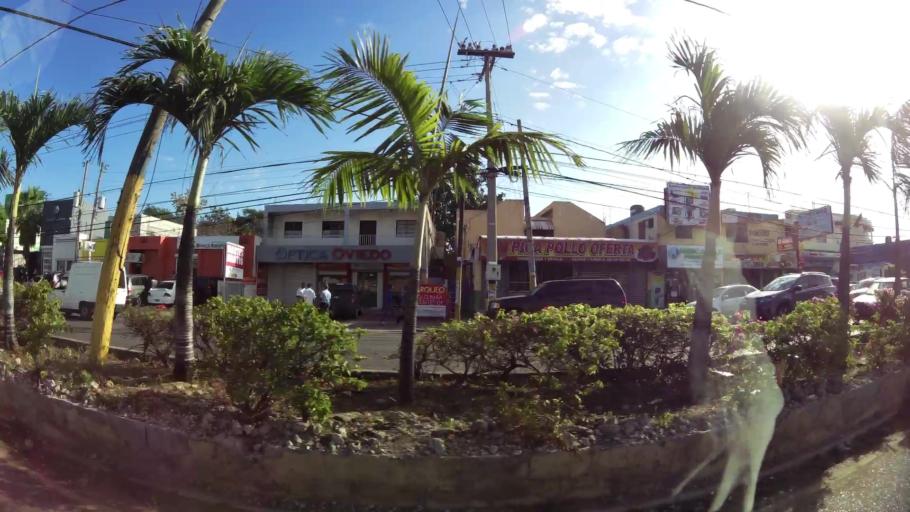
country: DO
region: Santo Domingo
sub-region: Santo Domingo
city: Santo Domingo Este
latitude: 18.5041
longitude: -69.8560
